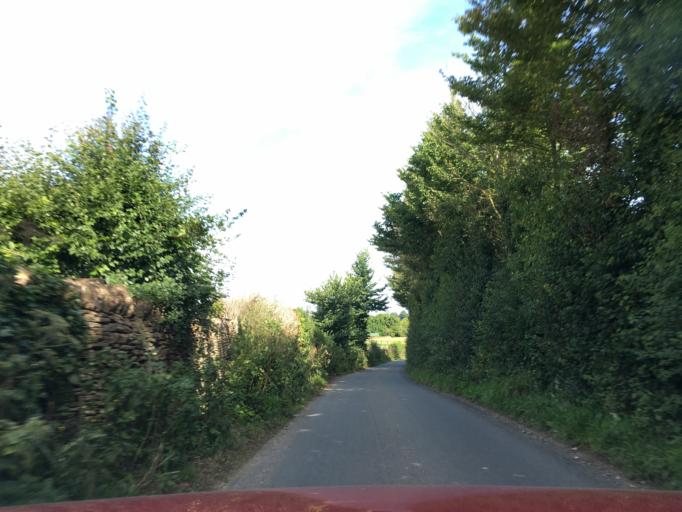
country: GB
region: England
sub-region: Wiltshire
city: Nettleton
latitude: 51.5061
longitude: -2.2611
